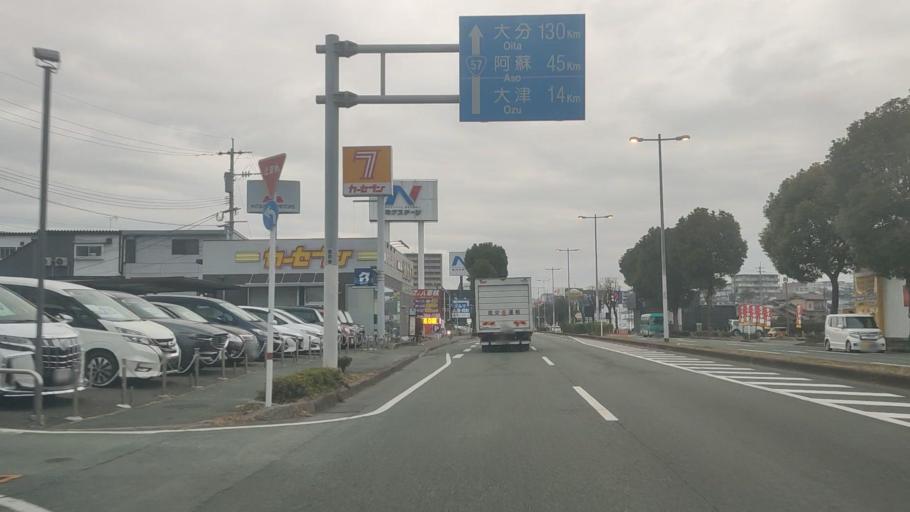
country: JP
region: Kumamoto
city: Kumamoto
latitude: 32.8171
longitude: 130.7524
